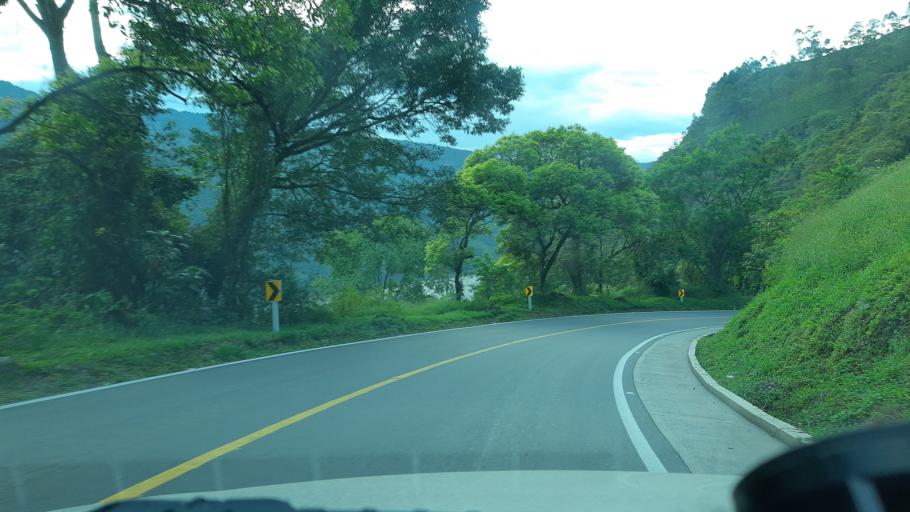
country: CO
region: Boyaca
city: Chivor
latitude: 4.9778
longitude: -73.3342
